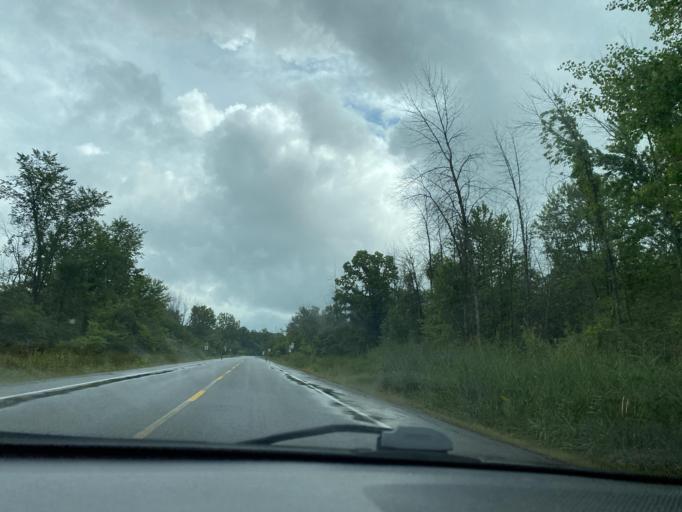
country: CA
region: Quebec
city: Baie-D'Urfe
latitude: 45.4456
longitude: -73.9179
